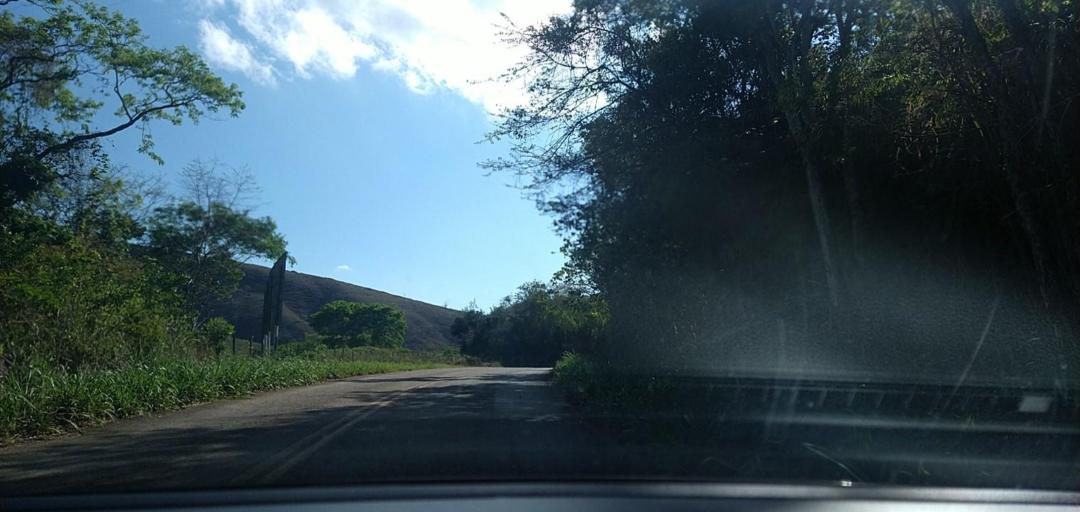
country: BR
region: Minas Gerais
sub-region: Alvinopolis
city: Alvinopolis
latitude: -20.1749
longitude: -42.9242
